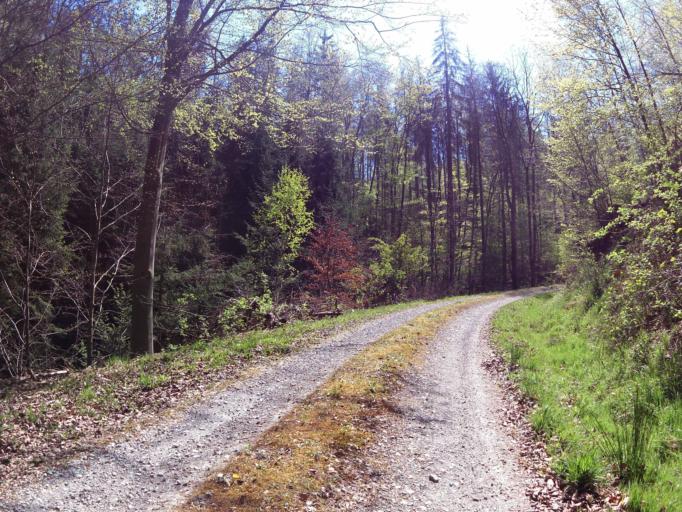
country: DE
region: Thuringia
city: Krauthausen
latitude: 50.9782
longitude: 10.2413
